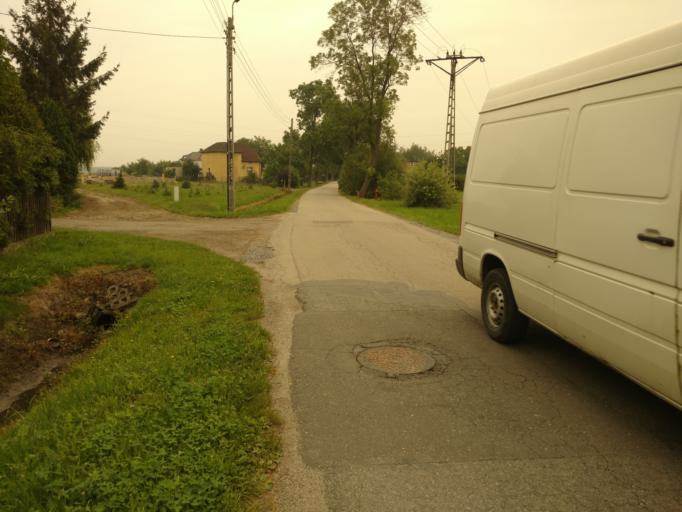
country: PL
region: Silesian Voivodeship
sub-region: Powiat pszczynski
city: Pszczyna
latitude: 49.9939
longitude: 18.9587
